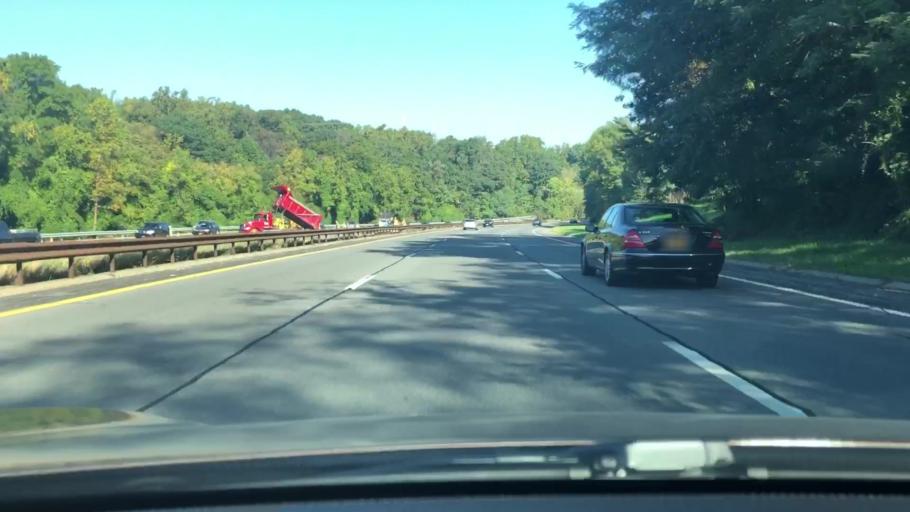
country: US
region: New York
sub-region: Westchester County
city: Ardsley
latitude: 41.0102
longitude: -73.8294
